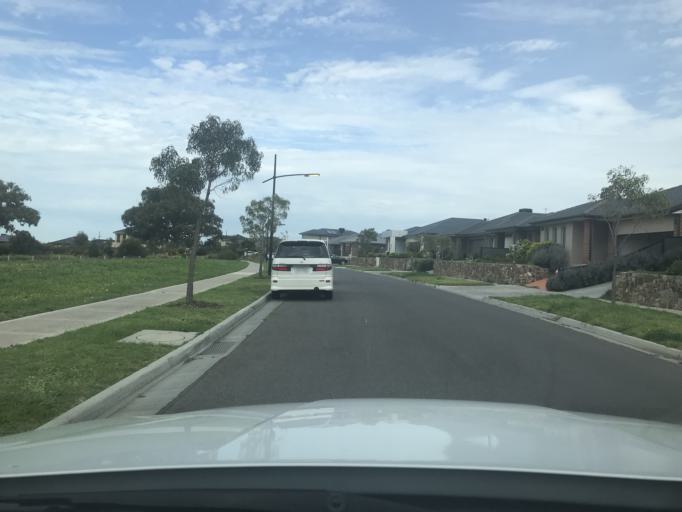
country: AU
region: Victoria
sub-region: Hume
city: Roxburgh Park
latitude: -37.5969
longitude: 144.8977
